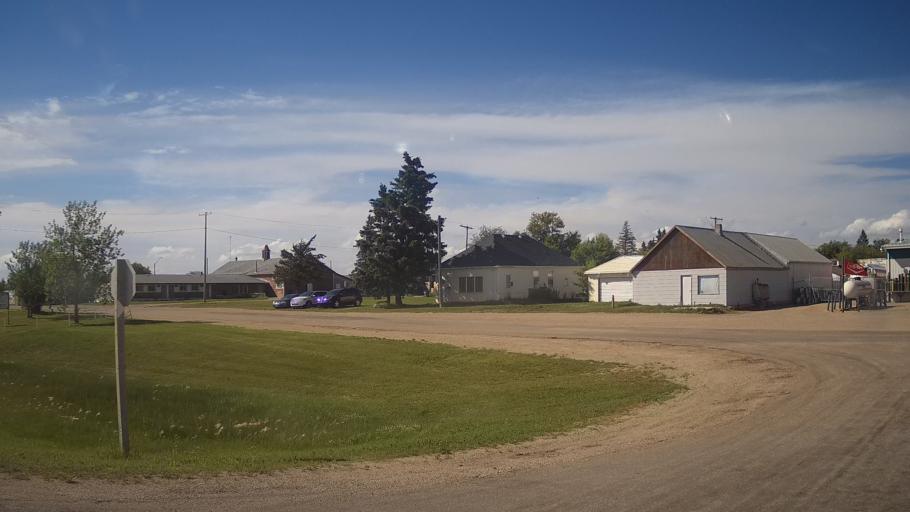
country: CA
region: Saskatchewan
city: Foam Lake
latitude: 51.2619
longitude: -103.7369
